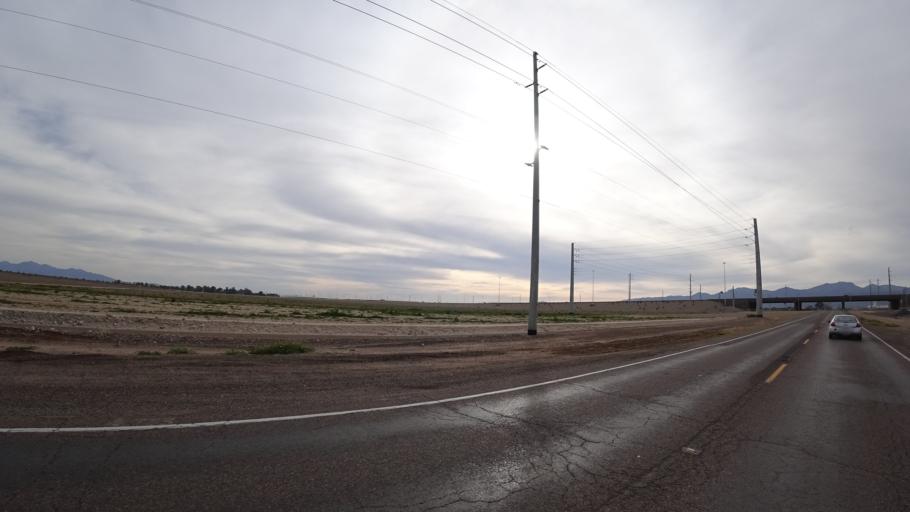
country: US
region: Arizona
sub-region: Maricopa County
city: Citrus Park
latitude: 33.5662
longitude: -112.4138
